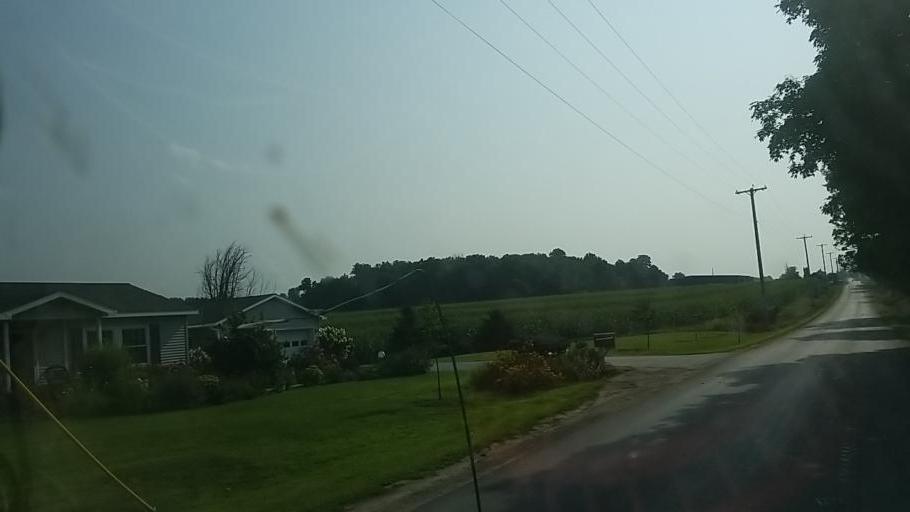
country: US
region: New York
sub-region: Montgomery County
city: Fonda
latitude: 42.9124
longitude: -74.3539
